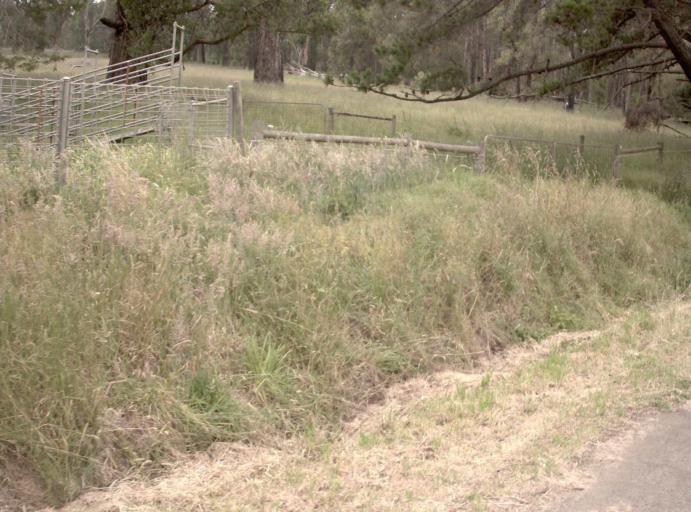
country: AU
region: Victoria
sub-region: Latrobe
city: Moe
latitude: -38.3354
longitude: 146.2216
